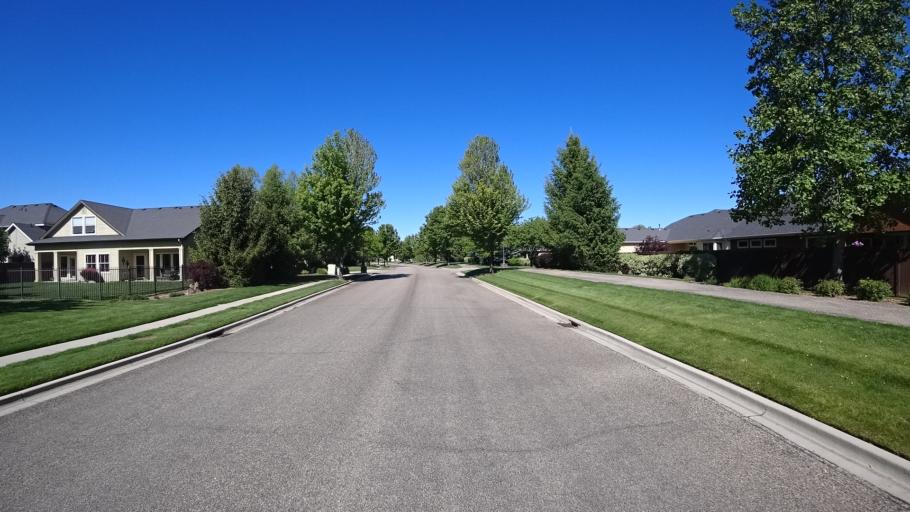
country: US
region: Idaho
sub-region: Ada County
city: Meridian
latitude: 43.6576
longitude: -116.4064
